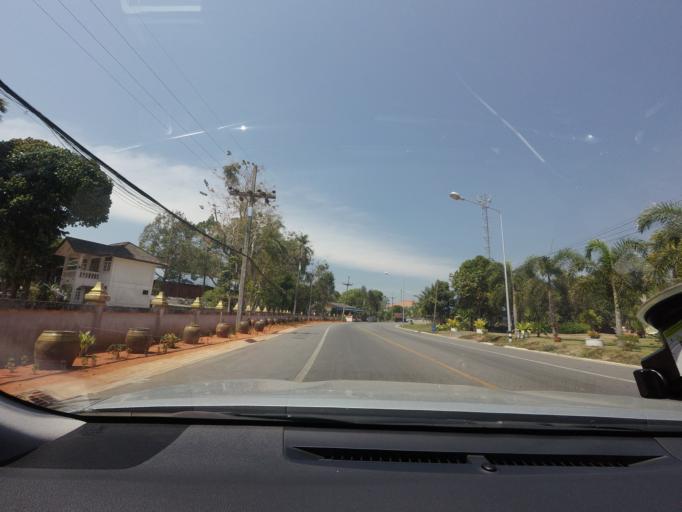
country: TH
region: Surat Thani
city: Tha Chang
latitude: 9.2578
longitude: 99.1901
